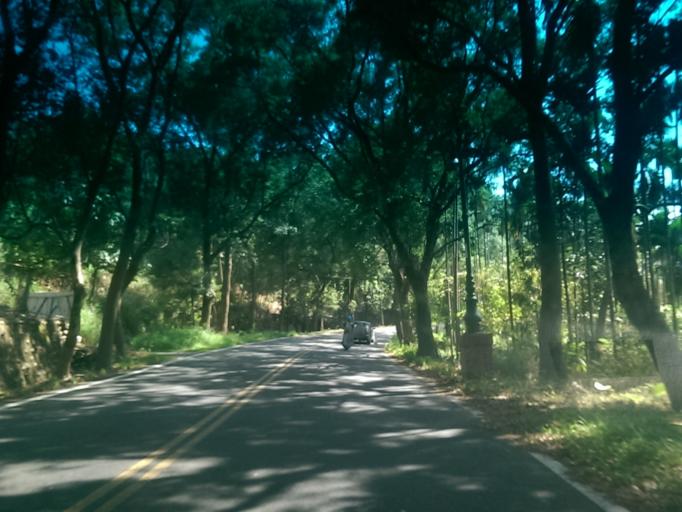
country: TW
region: Taiwan
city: Lugu
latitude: 23.8285
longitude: 120.7618
